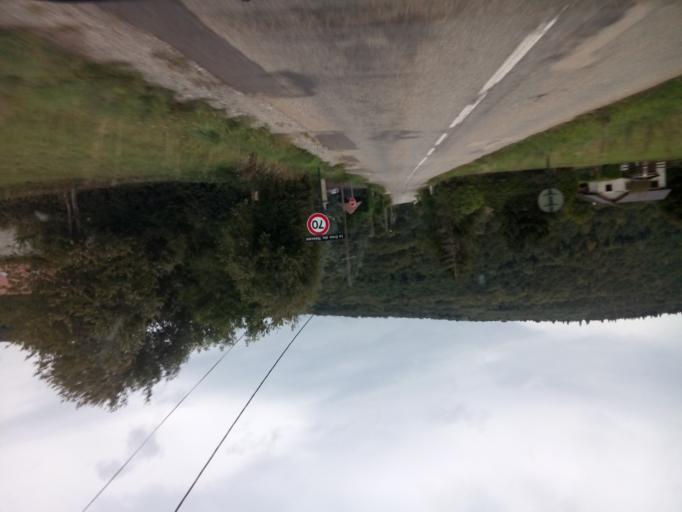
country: FR
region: Rhone-Alpes
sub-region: Departement de l'Isere
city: Pierre-Chatel
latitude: 44.9810
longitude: 5.7764
